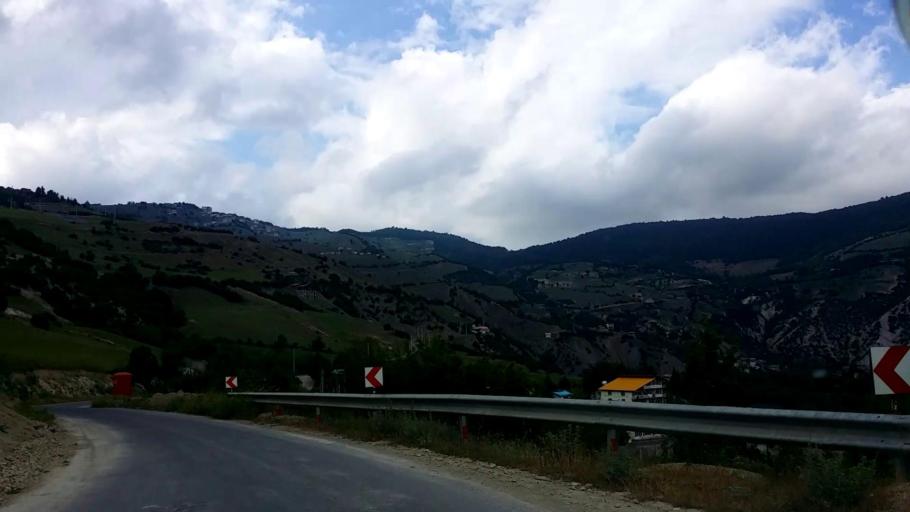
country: IR
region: Mazandaran
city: Chalus
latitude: 36.5421
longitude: 51.2727
